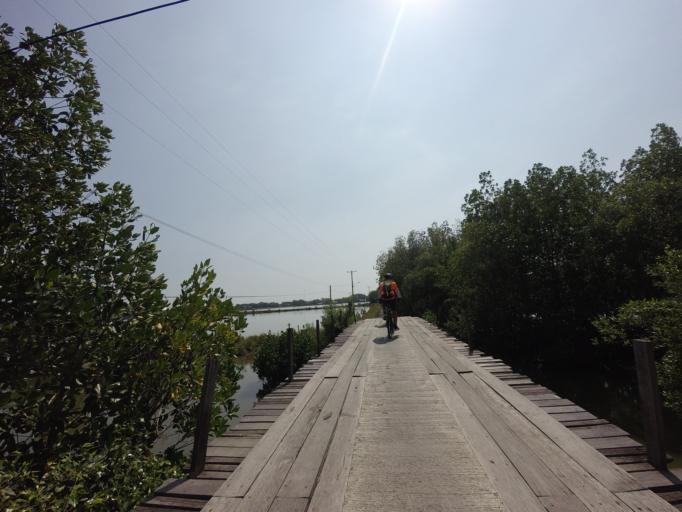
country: TH
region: Bangkok
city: Thung Khru
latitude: 13.5147
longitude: 100.4228
